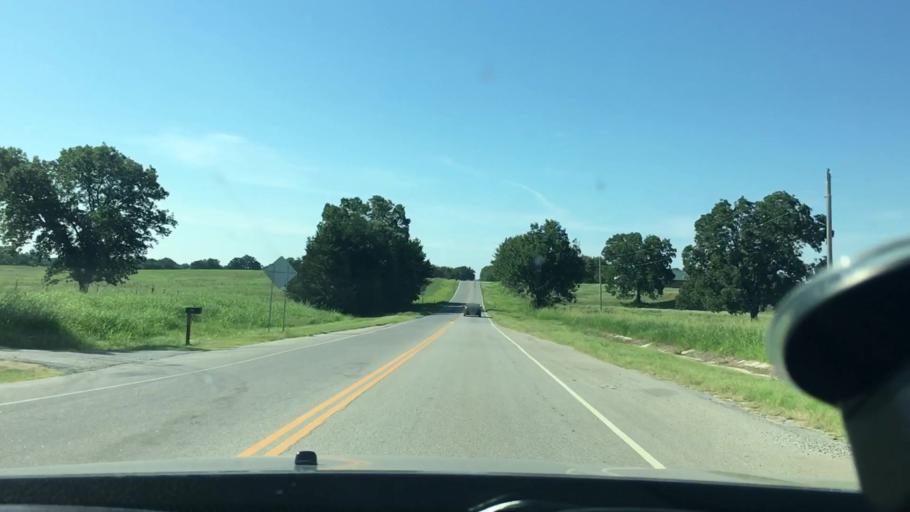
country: US
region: Oklahoma
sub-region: Johnston County
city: Tishomingo
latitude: 34.2735
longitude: -96.5488
